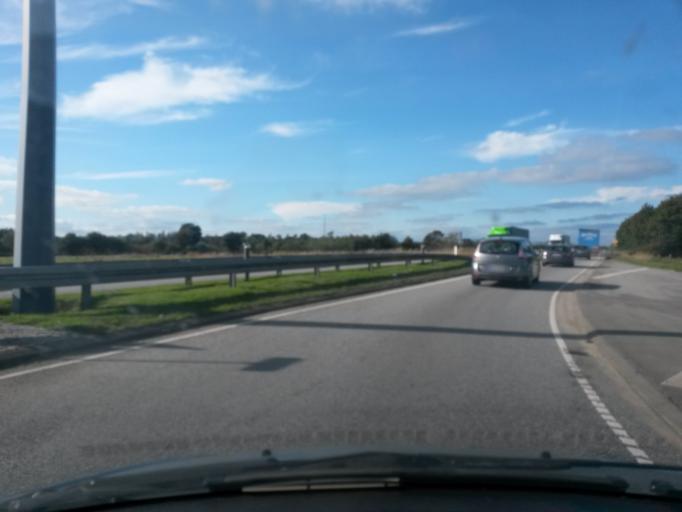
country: DK
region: Central Jutland
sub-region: Herning Kommune
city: Avlum
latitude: 56.2654
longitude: 8.7739
